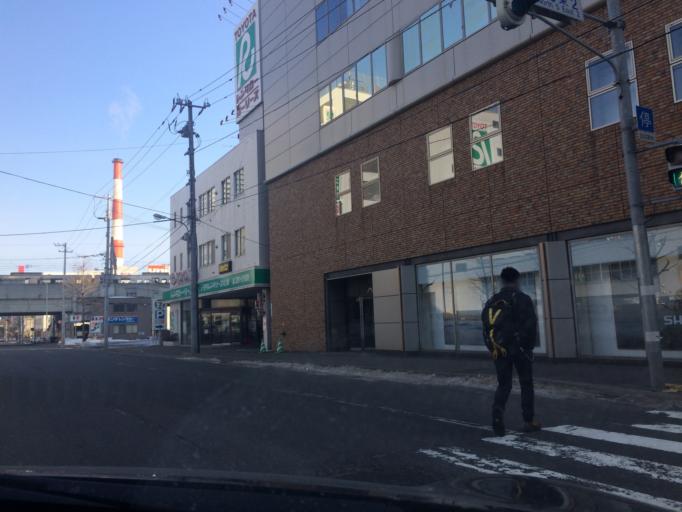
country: JP
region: Hokkaido
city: Sapporo
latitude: 43.0677
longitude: 141.3572
